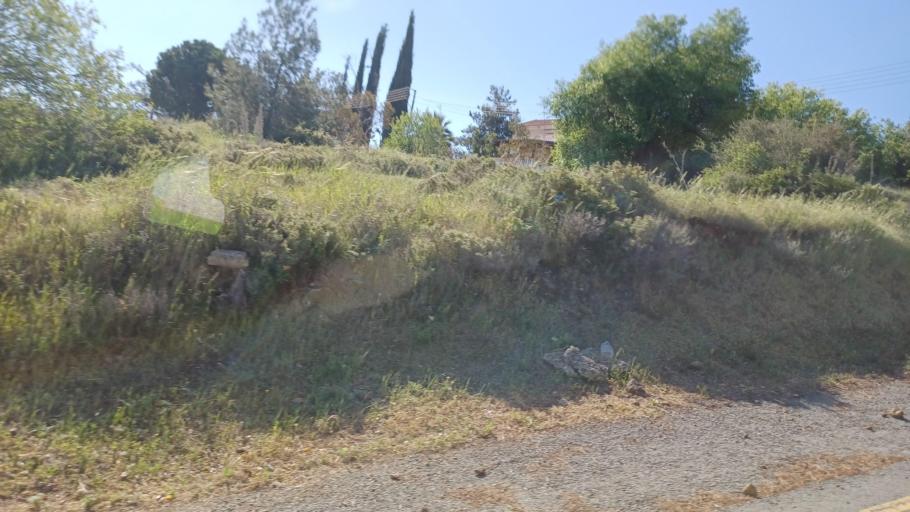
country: CY
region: Lefkosia
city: Peristerona
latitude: 35.0268
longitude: 33.0410
